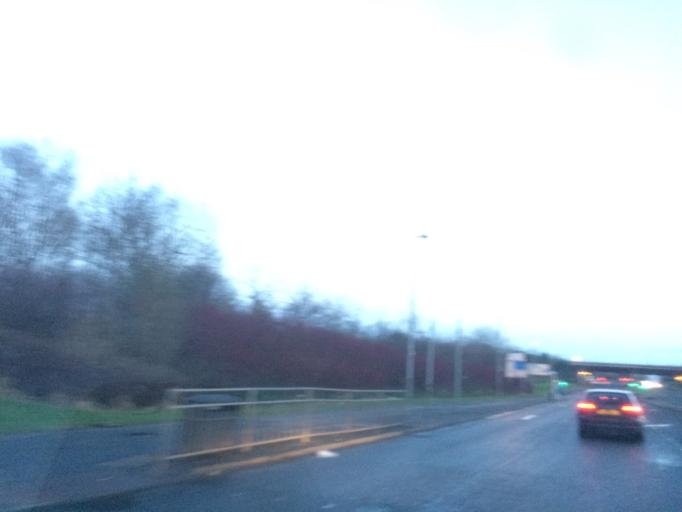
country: GB
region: Scotland
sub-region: East Renfrewshire
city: Newton Mearns
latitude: 55.8057
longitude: -4.3412
